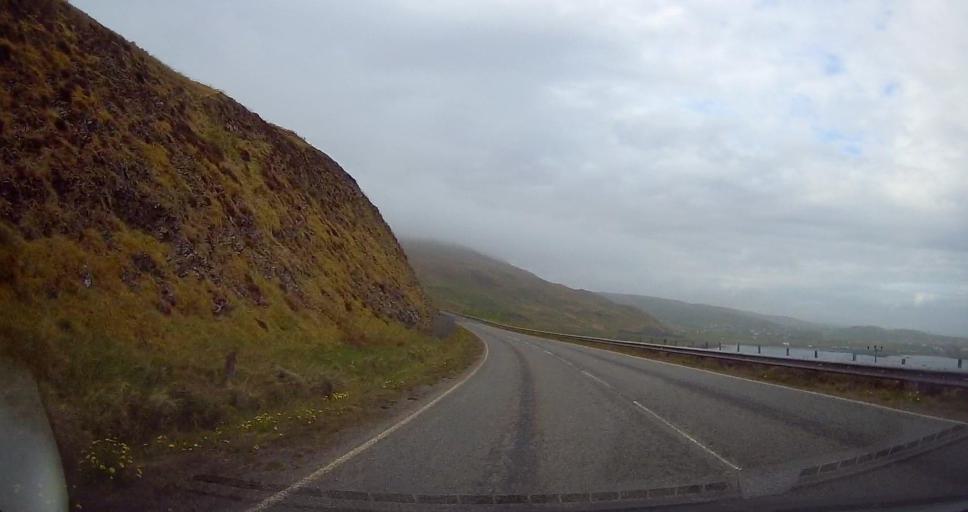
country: GB
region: Scotland
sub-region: Shetland Islands
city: Sandwick
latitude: 60.0191
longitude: -1.2314
